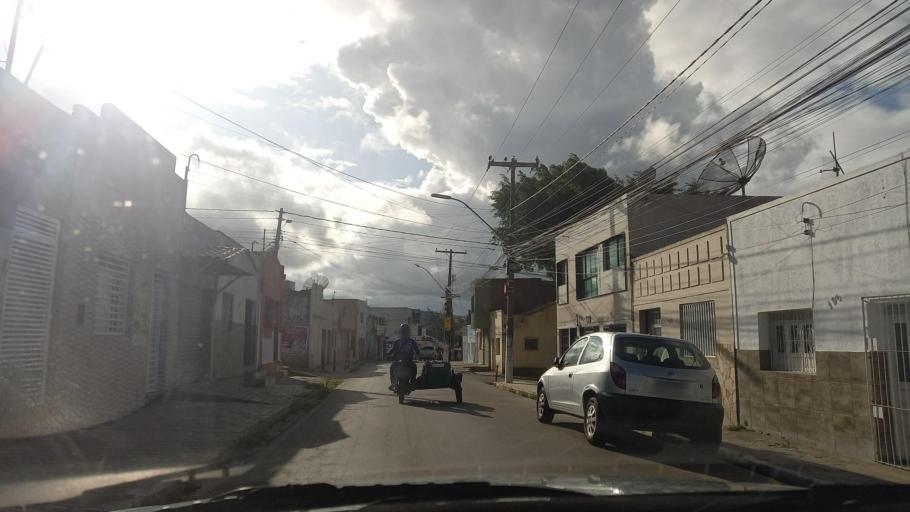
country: BR
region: Pernambuco
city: Garanhuns
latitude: -8.8973
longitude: -36.4935
